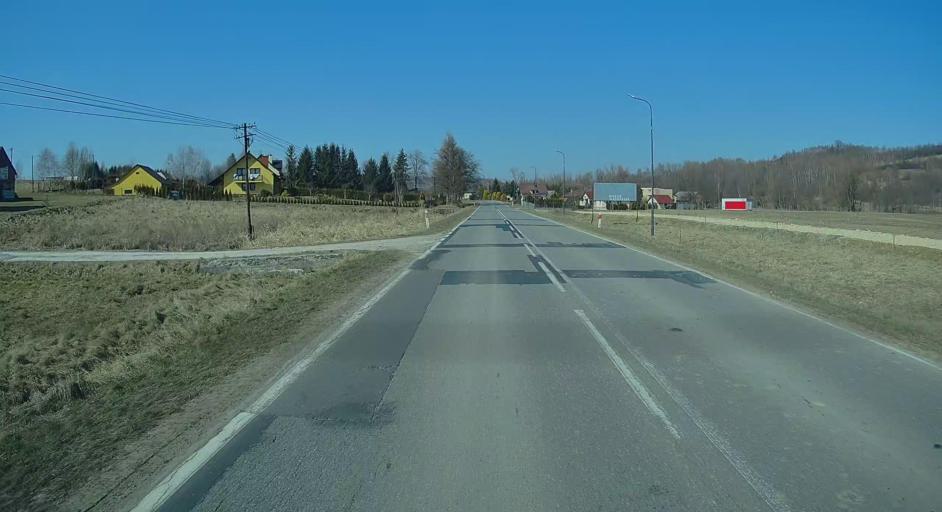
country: PL
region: Subcarpathian Voivodeship
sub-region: Powiat rzeszowski
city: Blazowa
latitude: 49.9353
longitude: 22.1102
